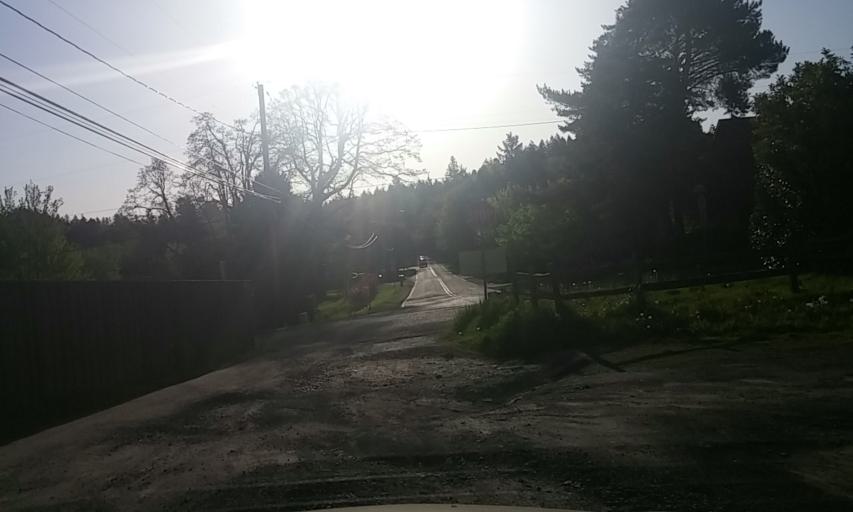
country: US
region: Oregon
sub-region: Washington County
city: Metzger
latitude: 45.4451
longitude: -122.7420
